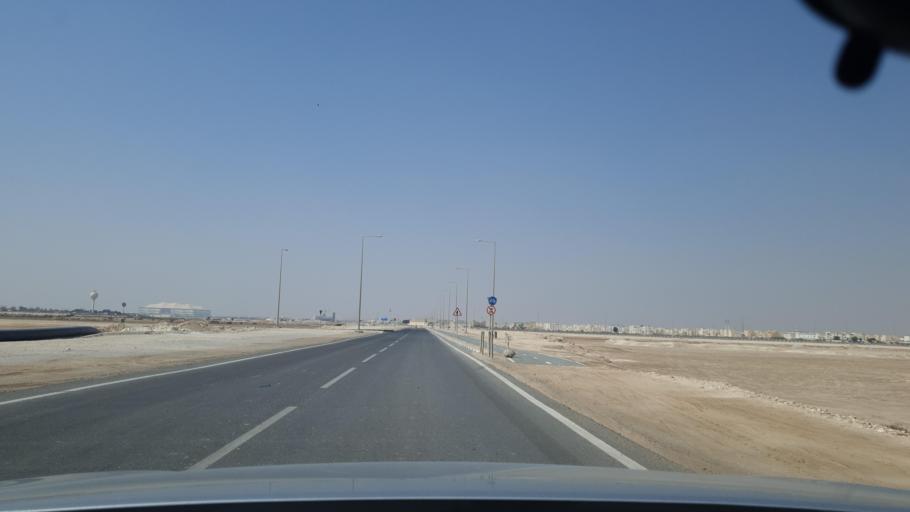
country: QA
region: Al Khawr
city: Al Khawr
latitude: 25.6682
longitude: 51.5291
